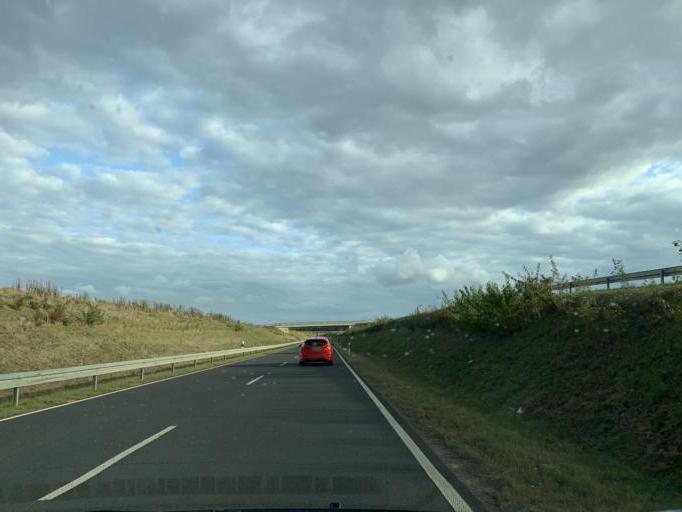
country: DE
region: North Rhine-Westphalia
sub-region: Regierungsbezirk Koln
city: Aldenhoven
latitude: 50.9199
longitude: 6.3118
